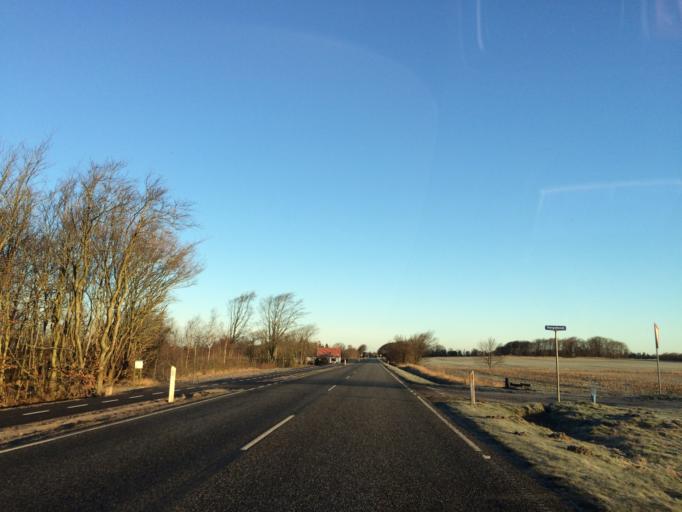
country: DK
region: Central Jutland
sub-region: Holstebro Kommune
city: Ulfborg
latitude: 56.3074
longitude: 8.3388
